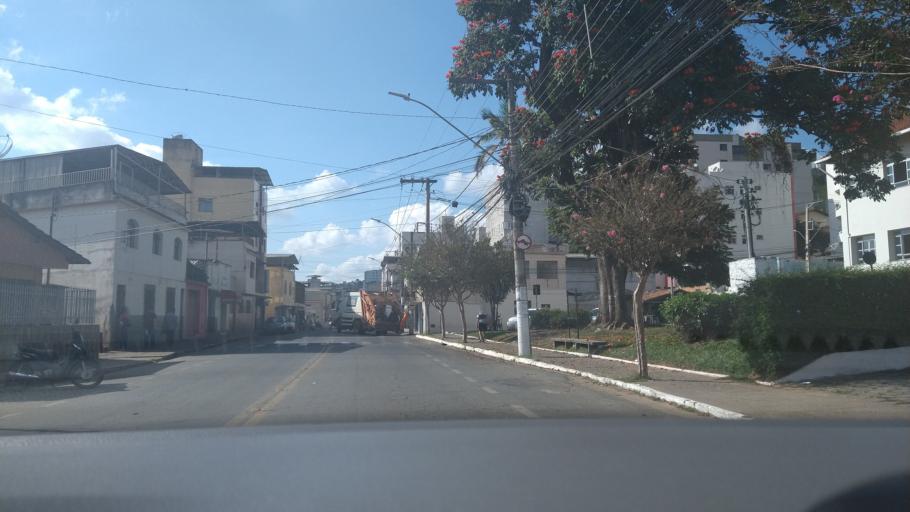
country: BR
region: Minas Gerais
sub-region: Vicosa
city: Vicosa
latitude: -20.7636
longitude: -42.8814
